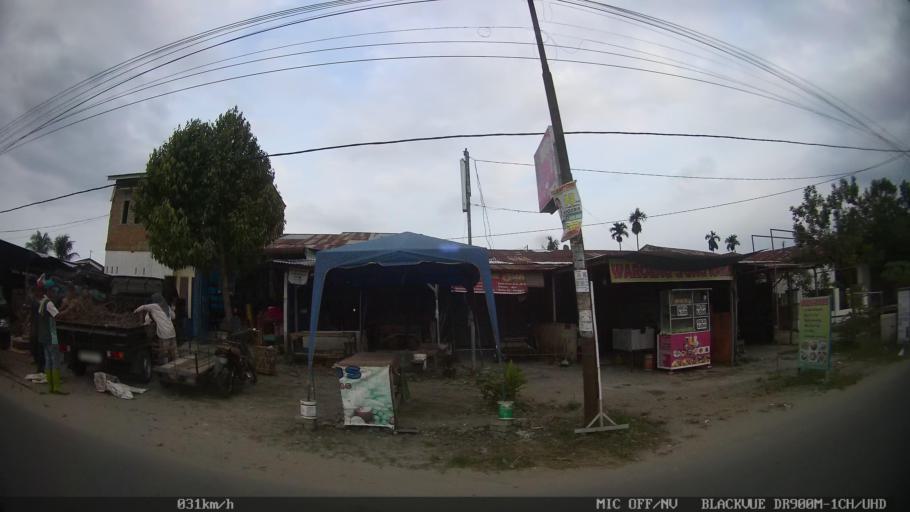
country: ID
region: North Sumatra
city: Sunggal
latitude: 3.5623
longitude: 98.5967
